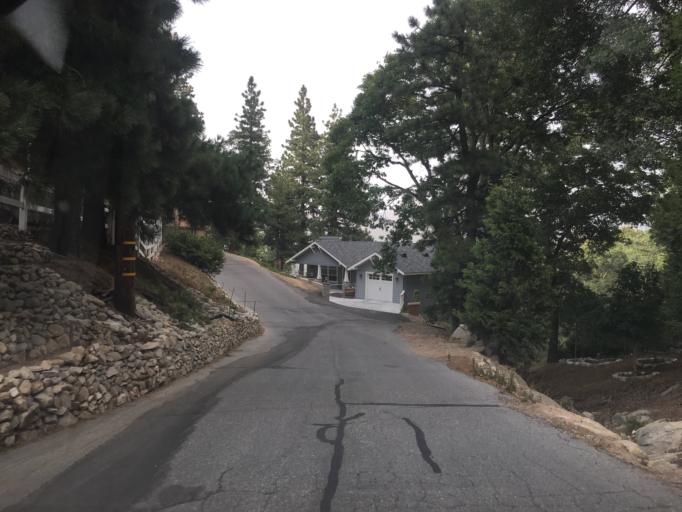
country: US
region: California
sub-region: San Bernardino County
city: Crestline
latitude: 34.2523
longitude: -117.2788
